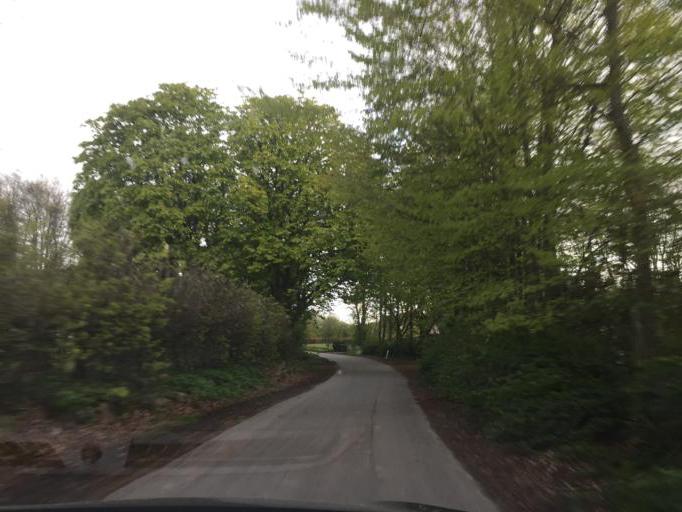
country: DK
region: Zealand
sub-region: Koge Kommune
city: Borup
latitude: 55.5202
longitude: 11.9898
